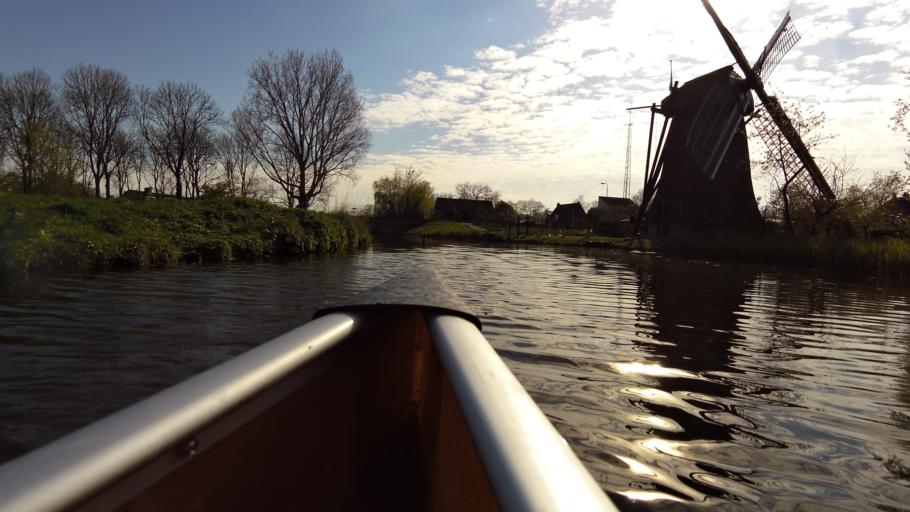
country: NL
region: South Holland
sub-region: Gemeente Lisse
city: Lisse
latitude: 52.2524
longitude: 4.5558
